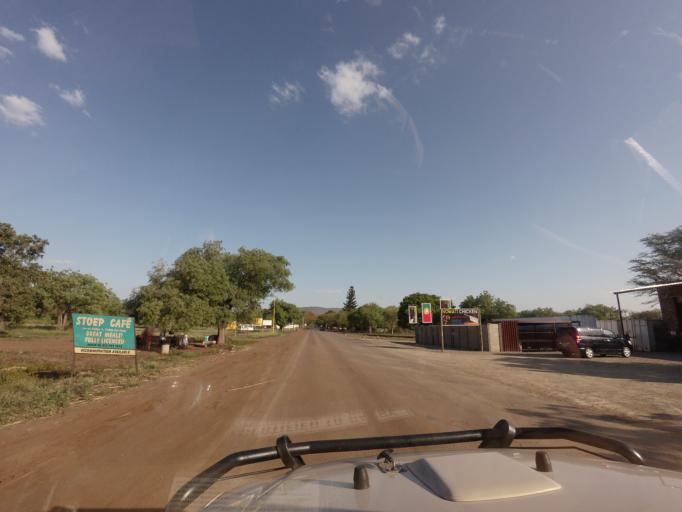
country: ZA
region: Mpumalanga
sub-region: Ehlanzeni District
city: Komatipoort
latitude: -25.4288
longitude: 31.9486
